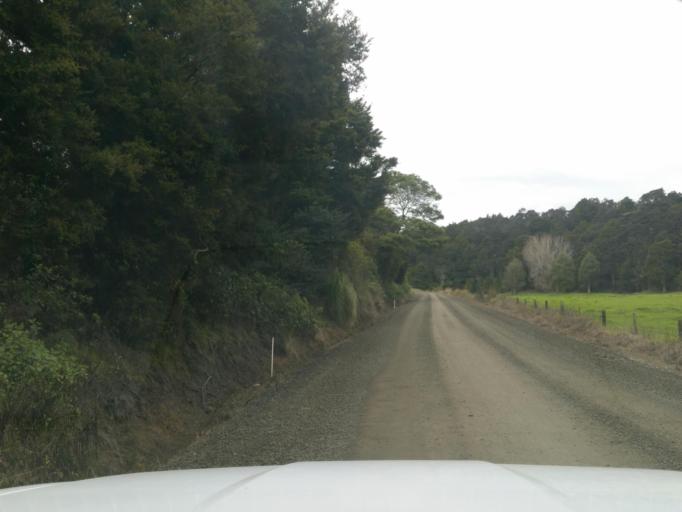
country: NZ
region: Northland
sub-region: Kaipara District
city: Dargaville
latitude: -35.7958
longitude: 173.9792
